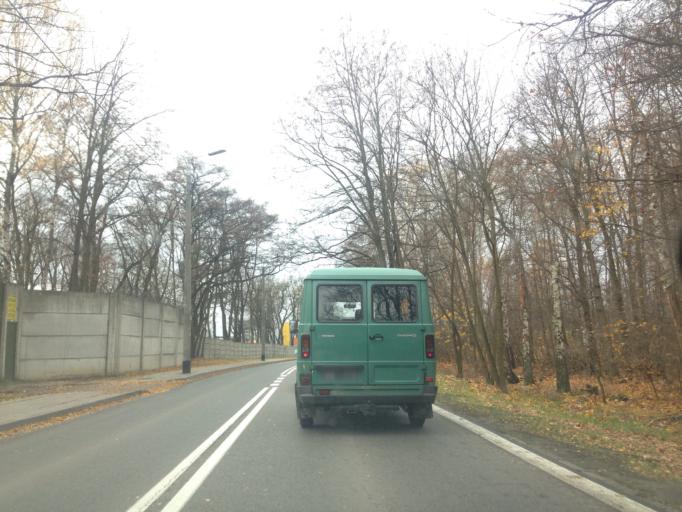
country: PL
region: Masovian Voivodeship
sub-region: Warszawa
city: Rembertow
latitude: 52.2455
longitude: 21.1405
